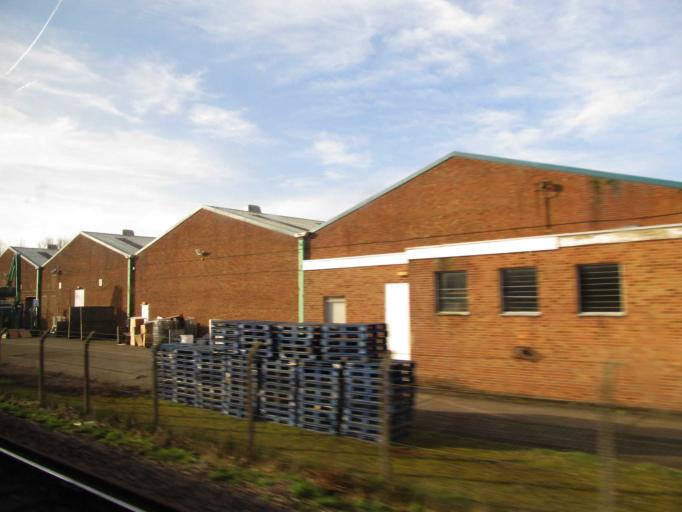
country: GB
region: England
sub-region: Surrey
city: Frimley
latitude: 51.3166
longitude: -0.7621
